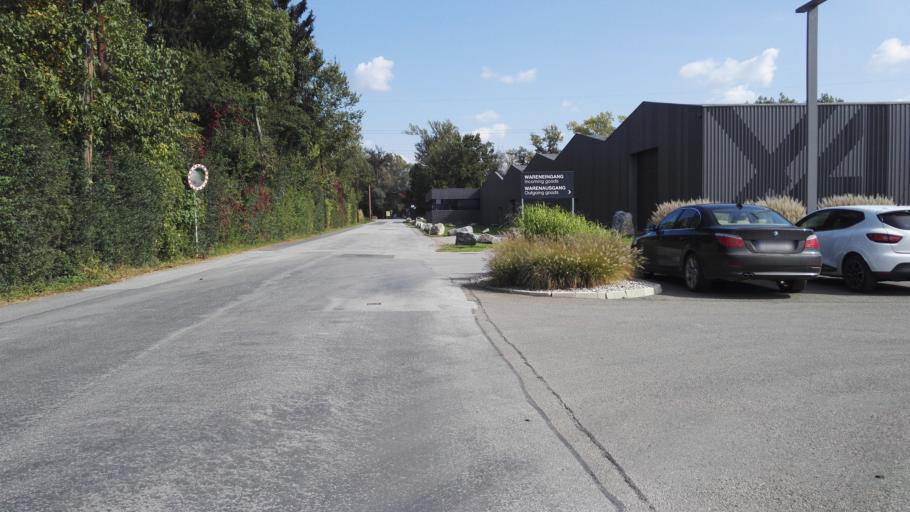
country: AT
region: Styria
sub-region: Politischer Bezirk Graz-Umgebung
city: Feldkirchen bei Graz
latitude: 47.0285
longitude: 15.4491
